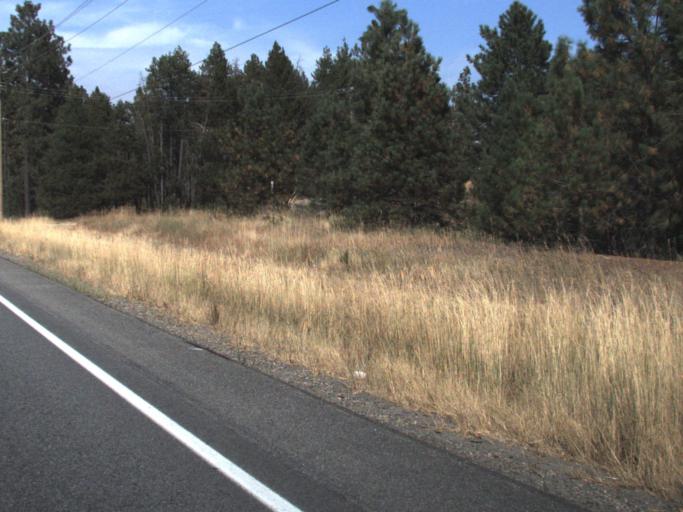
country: US
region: Washington
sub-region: Spokane County
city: Deer Park
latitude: 48.0131
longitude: -117.3495
